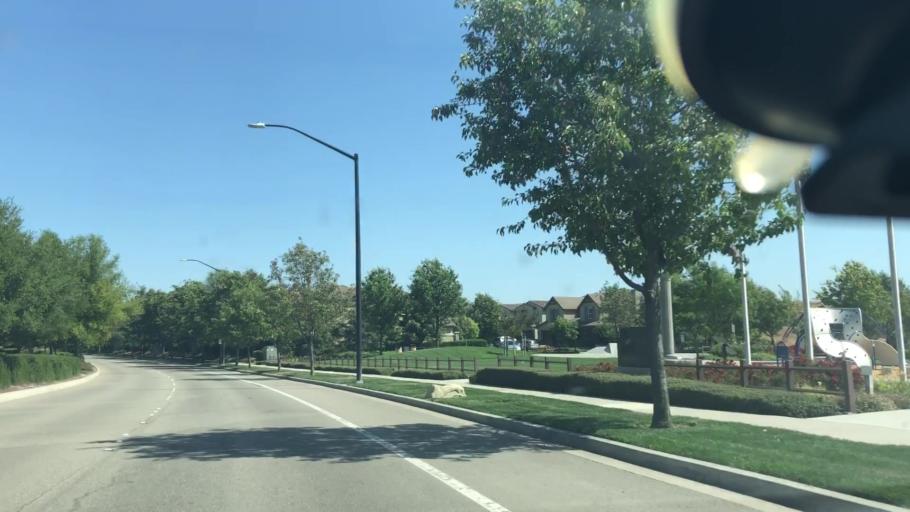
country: US
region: California
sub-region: Alameda County
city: Dublin
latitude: 37.7452
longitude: -121.8894
